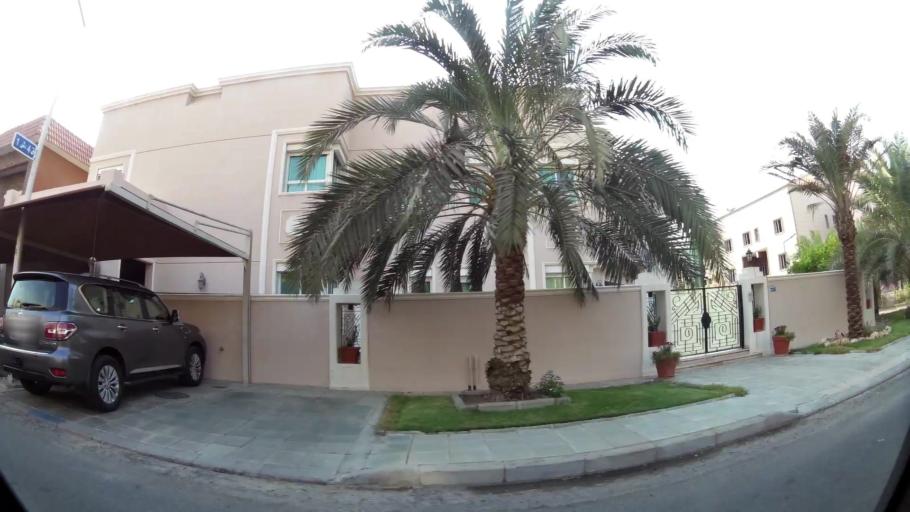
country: KW
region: Muhafazat Hawalli
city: Hawalli
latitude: 29.3084
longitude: 48.0003
